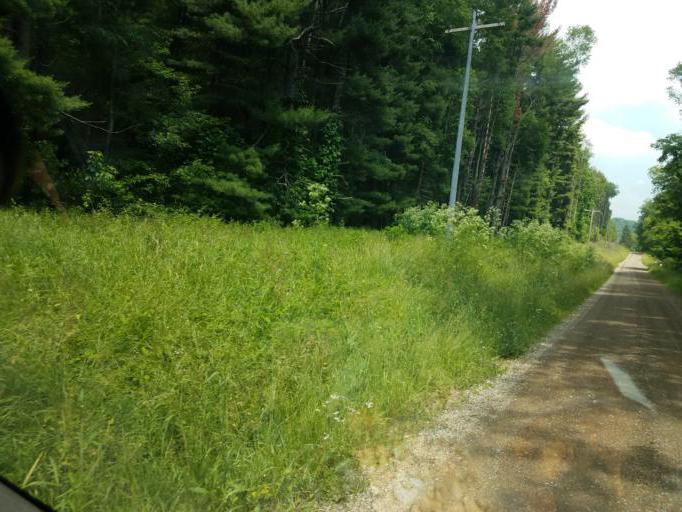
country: US
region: Ohio
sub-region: Knox County
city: Oak Hill
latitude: 40.3560
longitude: -82.2547
